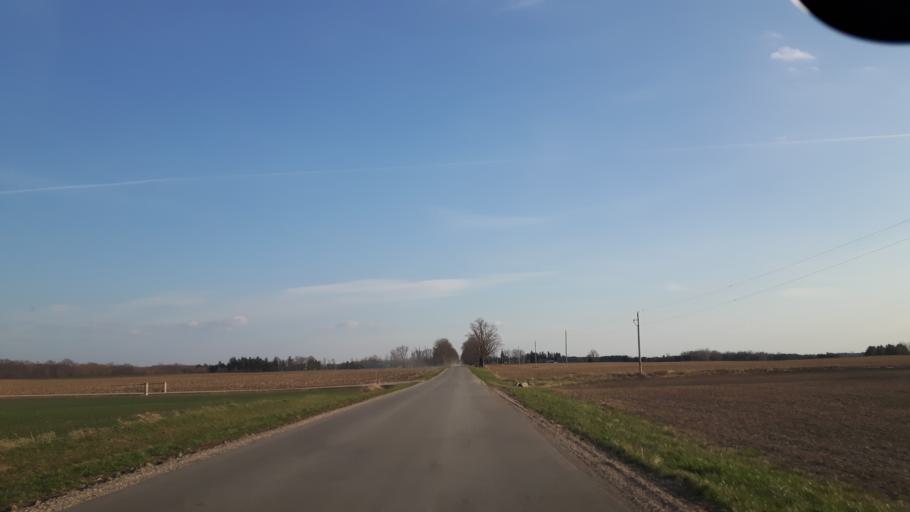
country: CA
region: Ontario
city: Goderich
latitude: 43.6326
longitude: -81.6643
